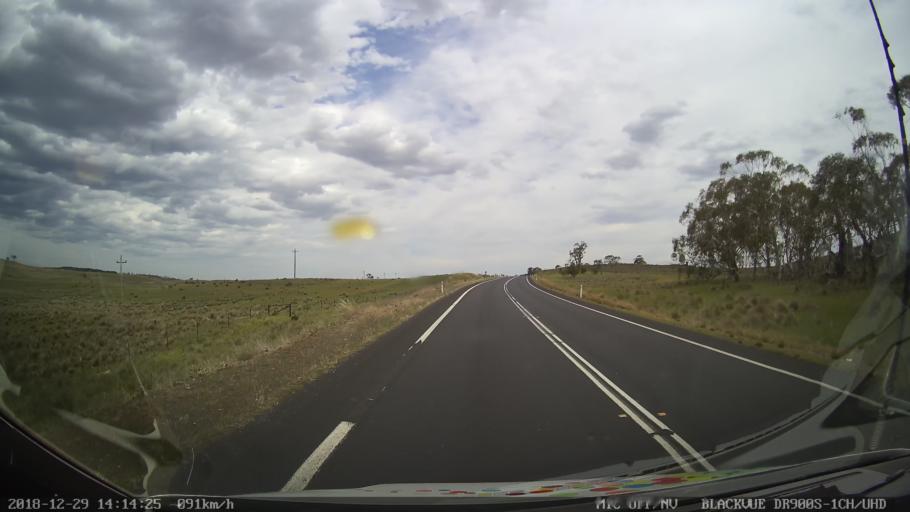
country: AU
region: New South Wales
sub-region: Cooma-Monaro
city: Cooma
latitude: -36.4420
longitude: 149.2378
